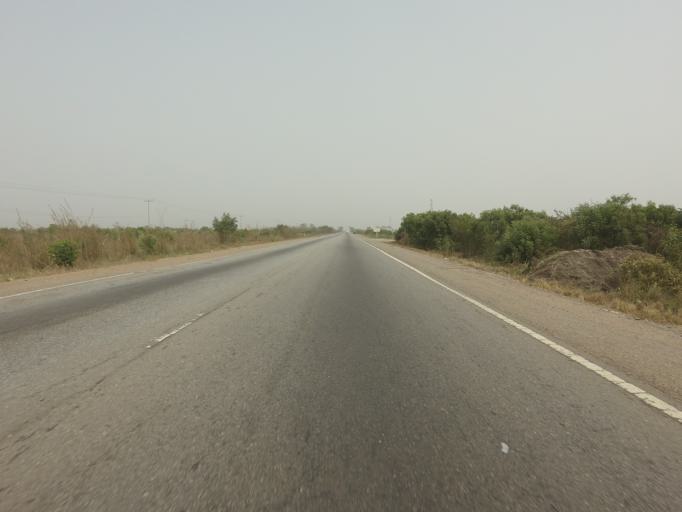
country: GH
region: Greater Accra
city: Tema
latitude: 5.7958
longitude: 0.1276
